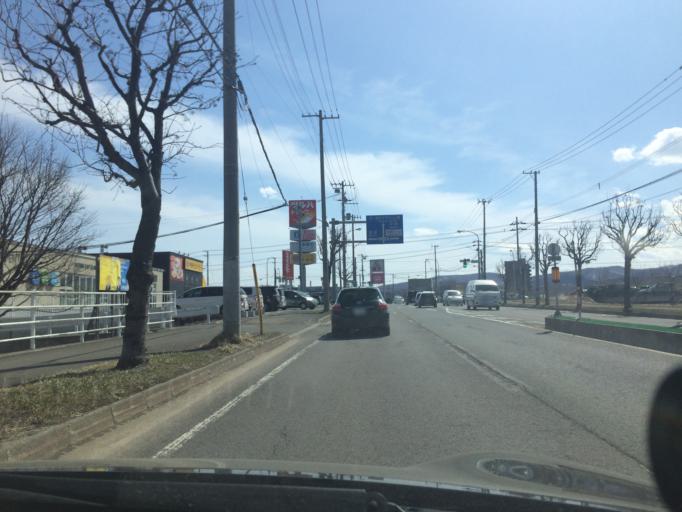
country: JP
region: Hokkaido
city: Sapporo
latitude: 42.9902
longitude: 141.4408
